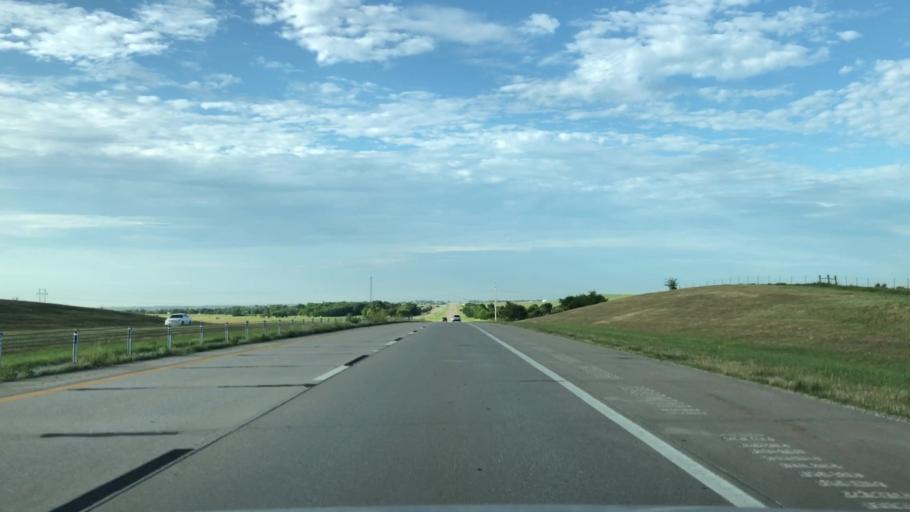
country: US
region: Oklahoma
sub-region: Osage County
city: Skiatook
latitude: 36.4071
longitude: -95.9206
